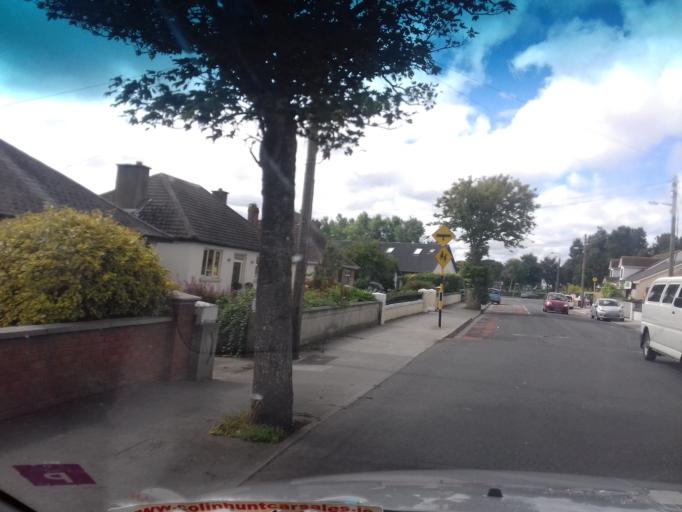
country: IE
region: Leinster
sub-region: Fingal County
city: Baldoyle
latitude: 53.3976
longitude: -6.1323
